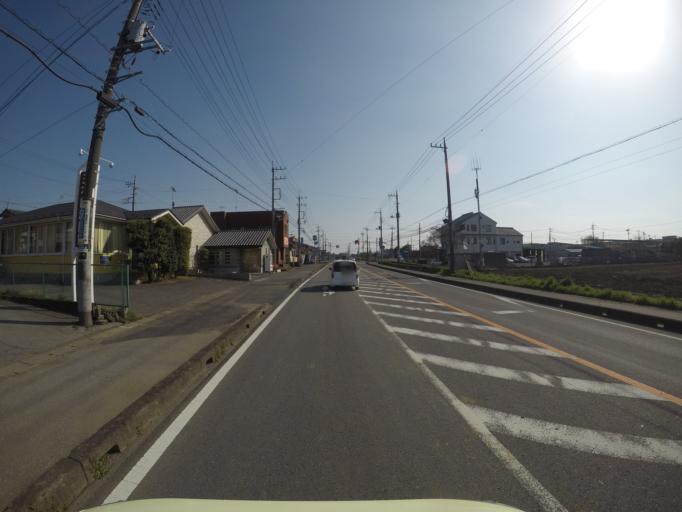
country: JP
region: Ibaraki
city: Yuki
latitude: 36.2727
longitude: 139.8786
